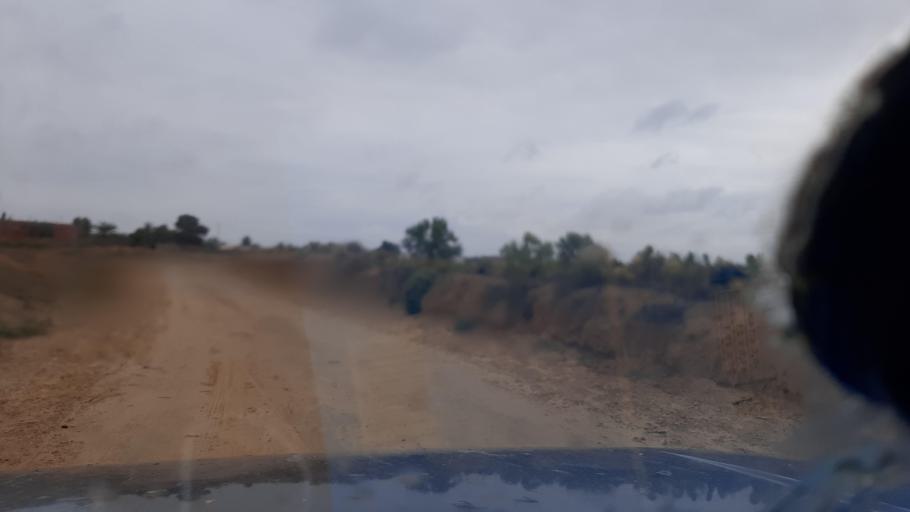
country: TN
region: Al Mahdiyah
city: Shurban
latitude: 35.4357
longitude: 10.4021
